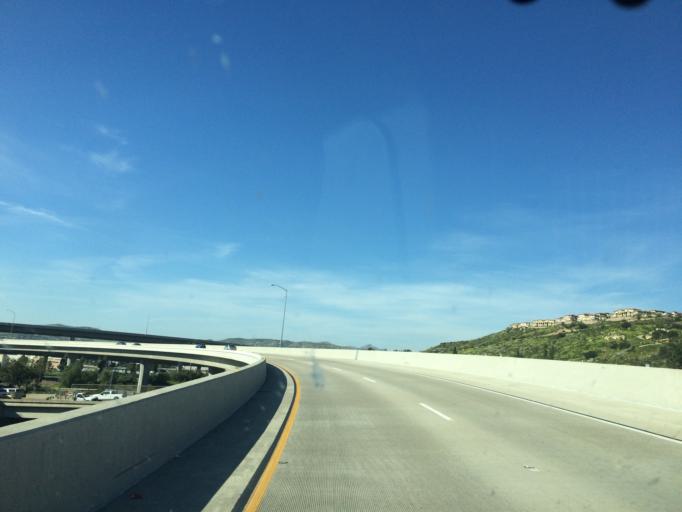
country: US
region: California
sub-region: San Diego County
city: Santee
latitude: 32.8298
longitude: -116.9616
